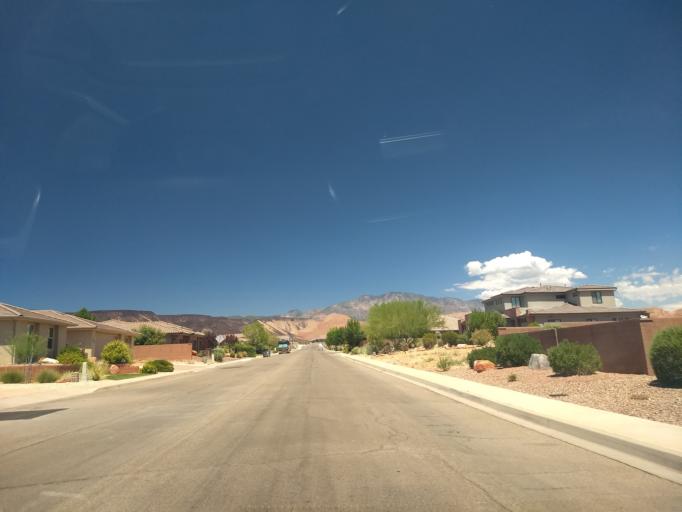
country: US
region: Utah
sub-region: Washington County
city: Washington
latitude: 37.1538
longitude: -113.5216
